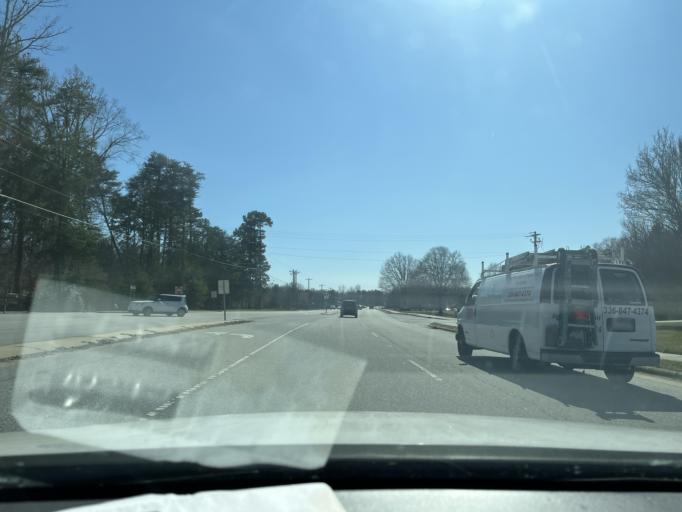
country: US
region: North Carolina
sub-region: Guilford County
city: Jamestown
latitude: 36.0276
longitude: -79.9232
